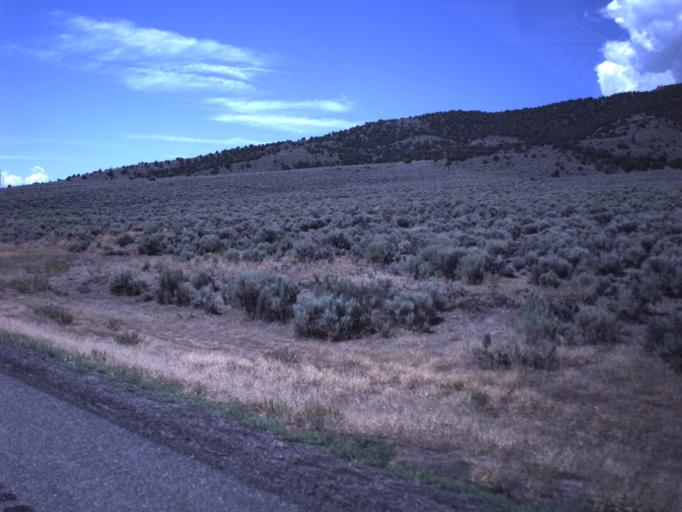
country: US
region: Utah
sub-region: Piute County
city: Junction
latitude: 38.3507
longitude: -112.2201
